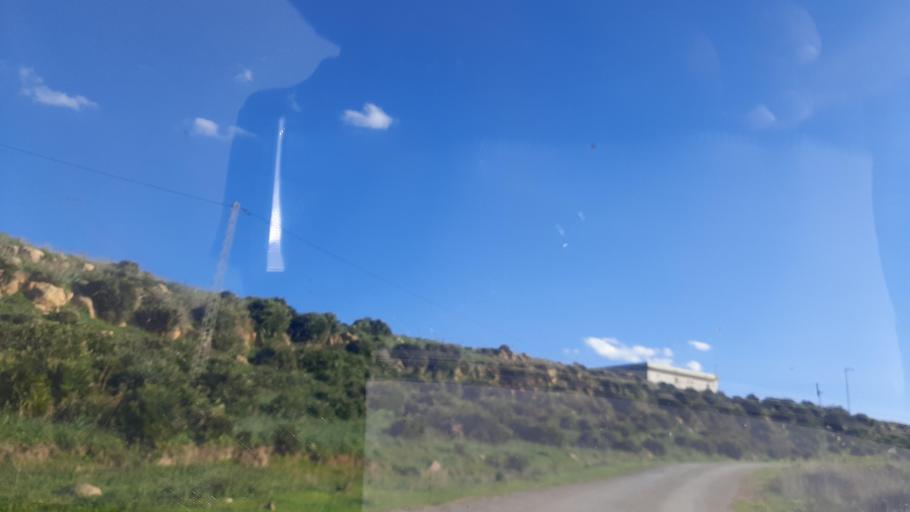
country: TN
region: Nabul
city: El Mida
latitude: 36.8100
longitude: 10.8456
